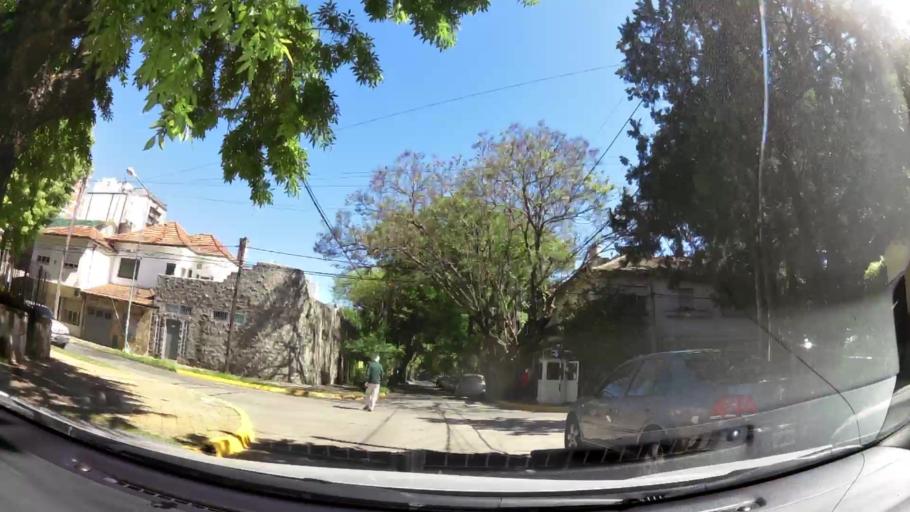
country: AR
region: Buenos Aires
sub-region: Partido de Vicente Lopez
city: Olivos
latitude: -34.5272
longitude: -58.4800
